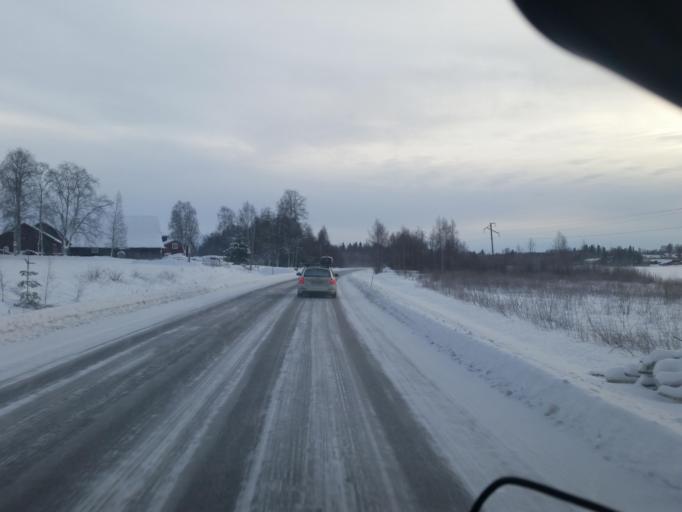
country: SE
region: Norrbotten
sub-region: Pitea Kommun
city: Norrfjarden
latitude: 65.4334
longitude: 21.4853
